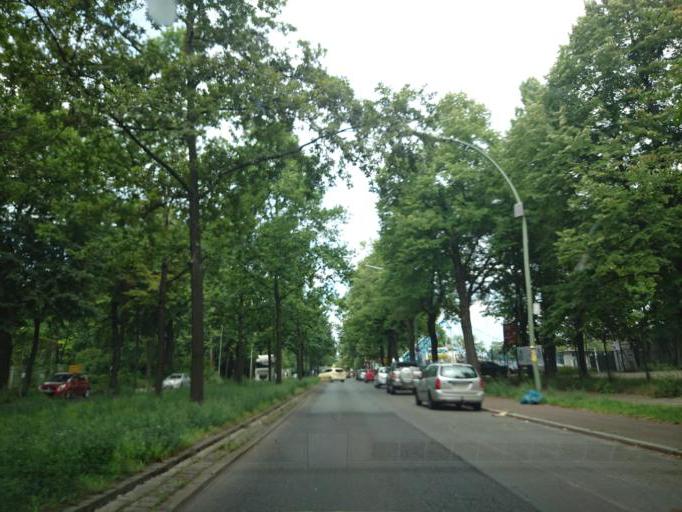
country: DE
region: Berlin
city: Lankwitz
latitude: 52.4312
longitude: 13.3539
